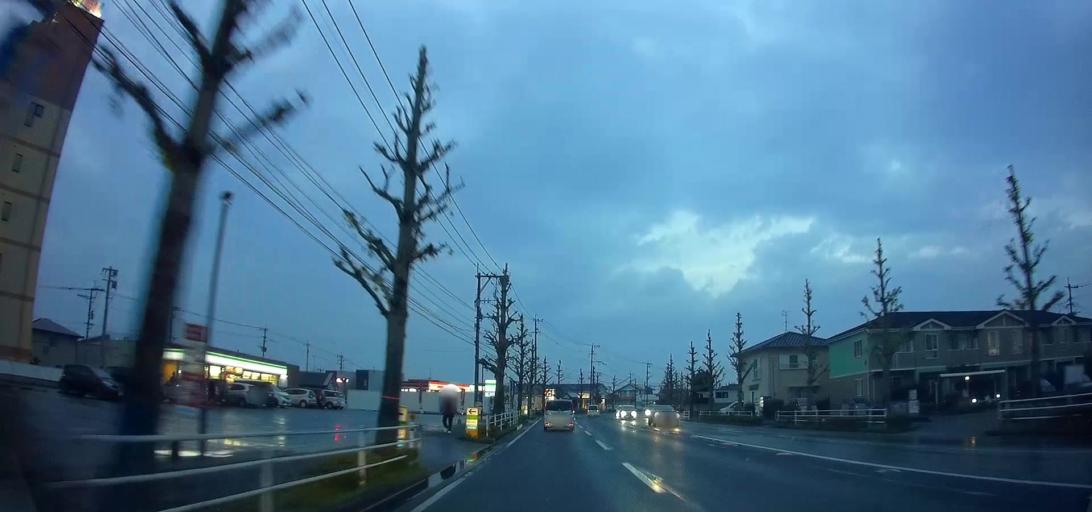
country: JP
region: Nagasaki
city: Omura
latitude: 32.9123
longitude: 129.9498
